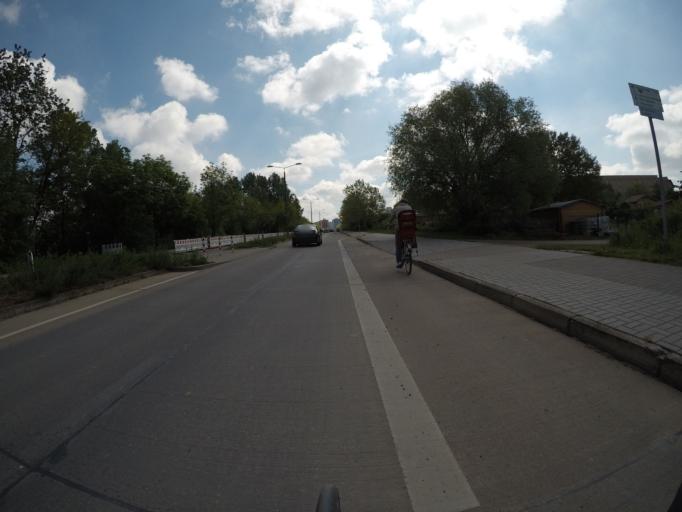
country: DE
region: Berlin
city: Kaulsdorf
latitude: 52.5254
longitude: 13.5796
